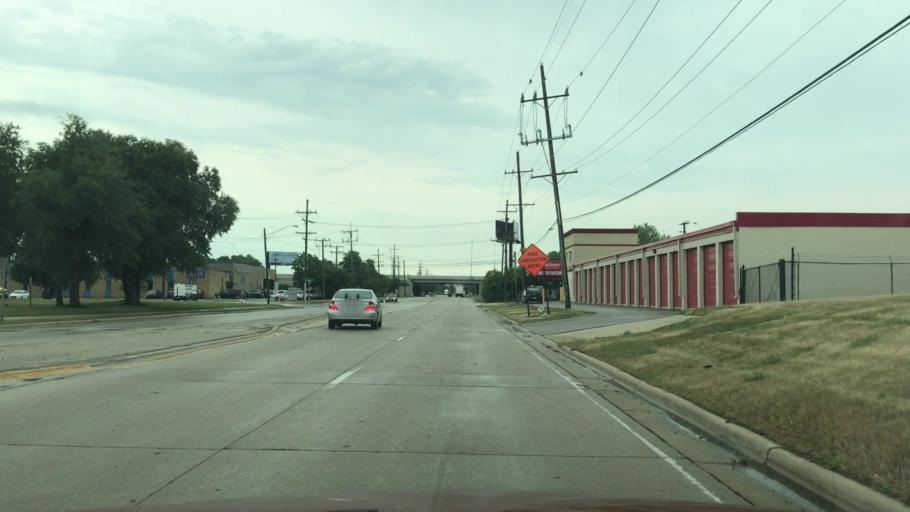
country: US
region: Illinois
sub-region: Cook County
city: Des Plaines
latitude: 42.0167
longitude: -87.9209
